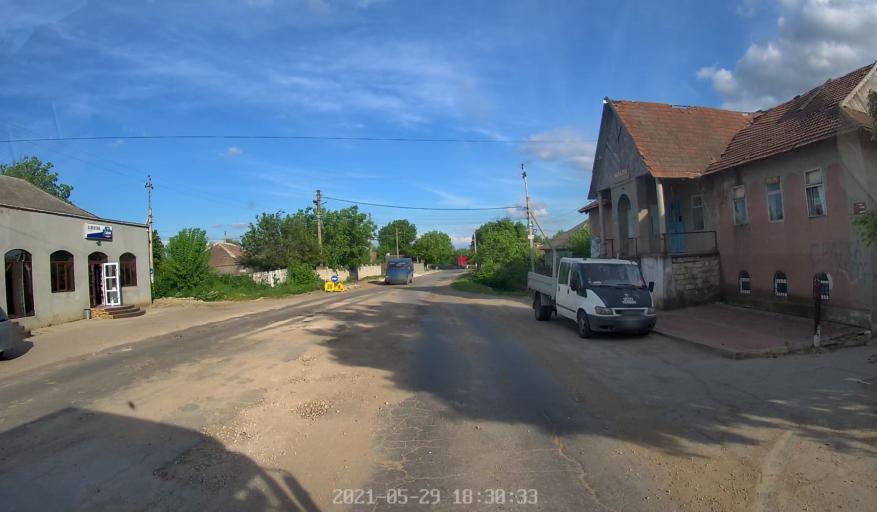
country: MD
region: Chisinau
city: Singera
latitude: 46.8221
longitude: 28.8790
